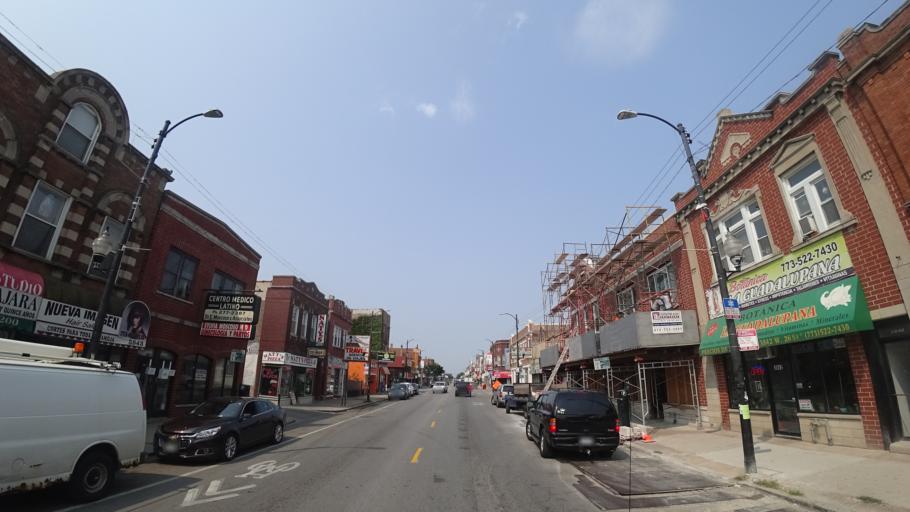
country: US
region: Illinois
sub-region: Cook County
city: Cicero
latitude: 41.8443
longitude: -87.7212
